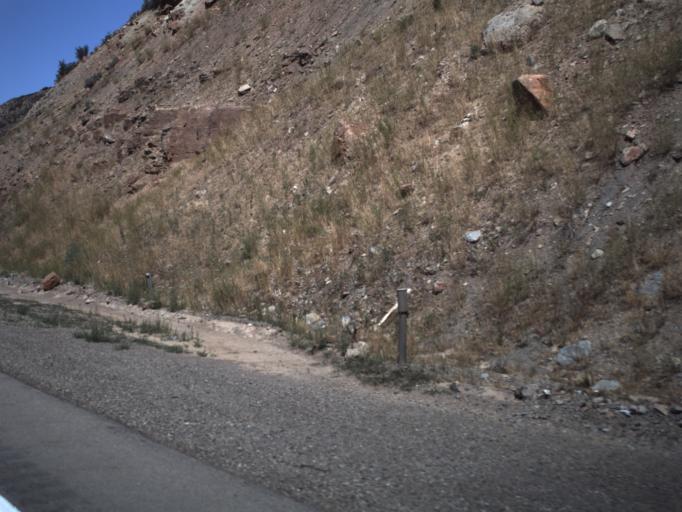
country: US
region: Utah
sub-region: Utah County
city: Mapleton
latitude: 40.0298
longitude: -111.5096
